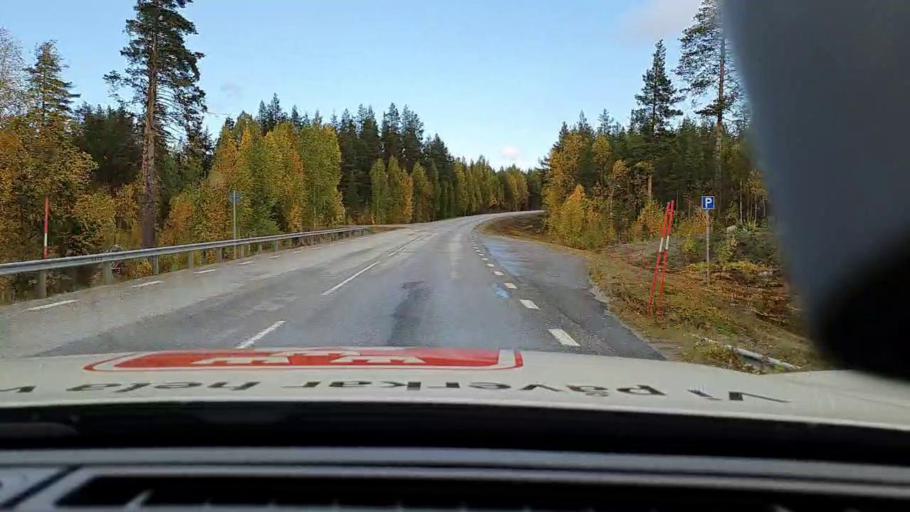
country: SE
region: Vaesterbotten
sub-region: Norsjo Kommun
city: Norsjoe
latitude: 64.9622
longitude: 19.6960
